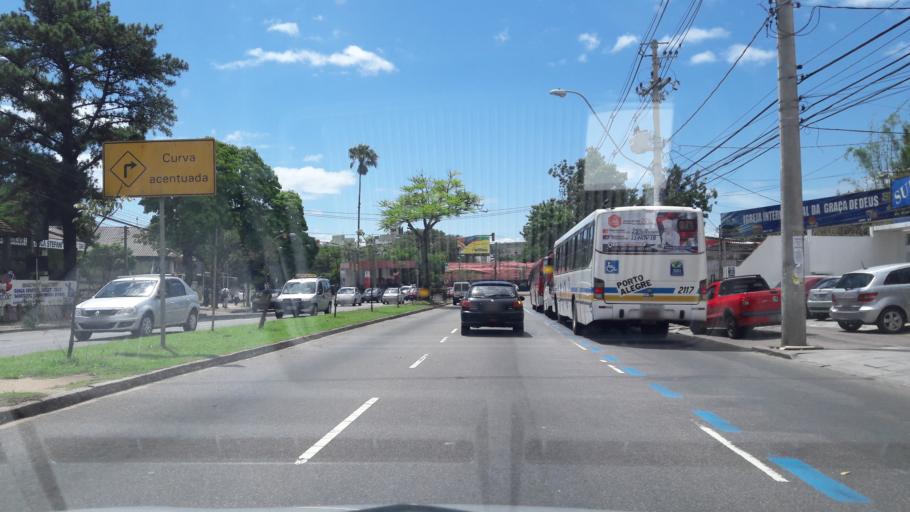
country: BR
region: Rio Grande do Sul
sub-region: Porto Alegre
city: Porto Alegre
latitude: -30.0988
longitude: -51.2314
